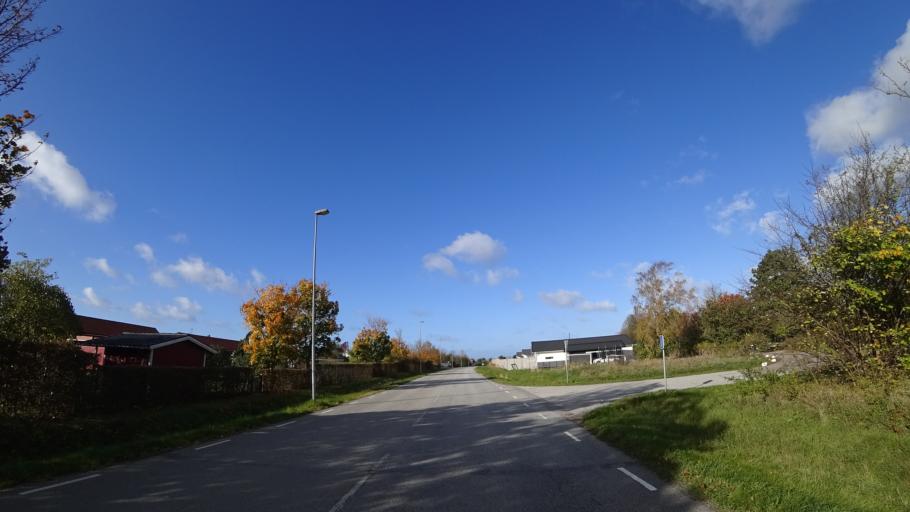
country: SE
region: Skane
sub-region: Staffanstorps Kommun
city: Hjaerup
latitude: 55.6749
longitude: 13.1493
